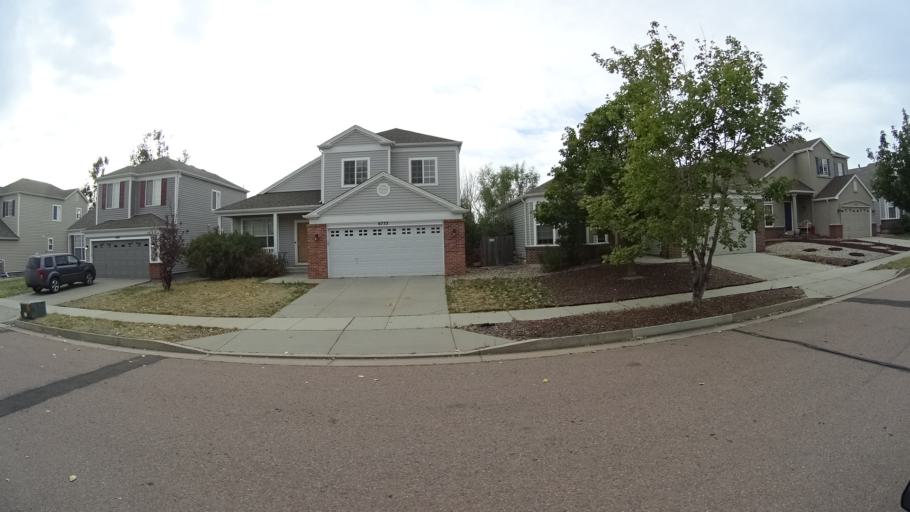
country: US
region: Colorado
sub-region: El Paso County
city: Cimarron Hills
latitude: 38.9134
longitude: -104.7046
